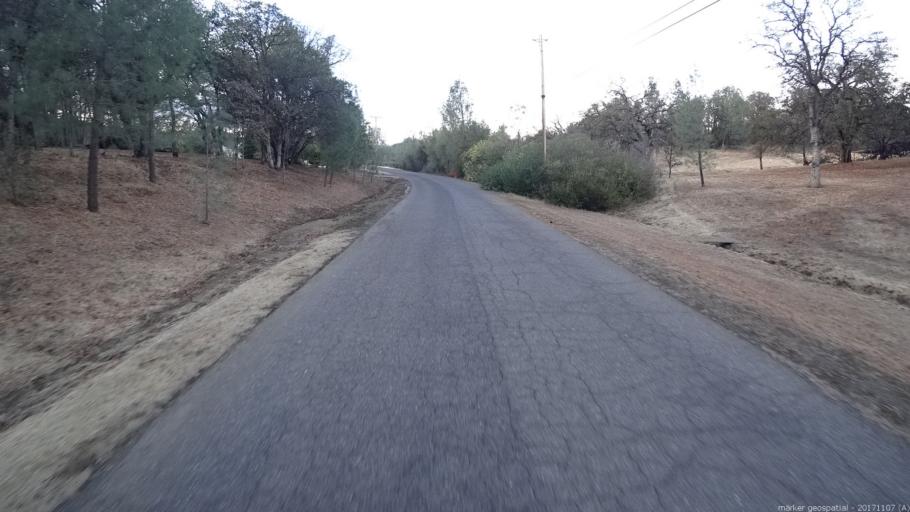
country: US
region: California
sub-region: Shasta County
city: Shasta
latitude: 40.5400
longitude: -122.4805
